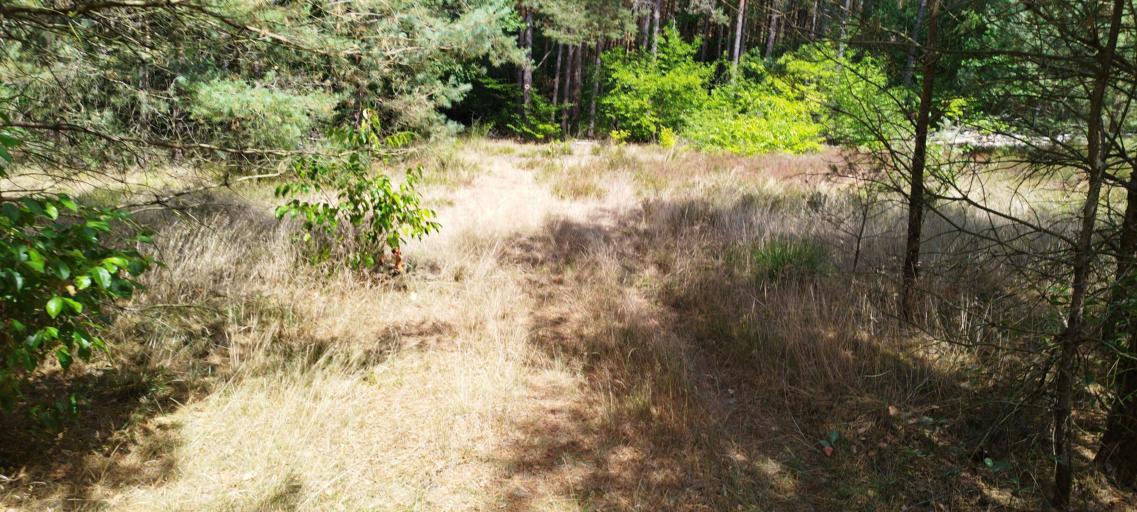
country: DE
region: Lower Saxony
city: Unterluss
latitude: 52.8321
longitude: 10.2157
